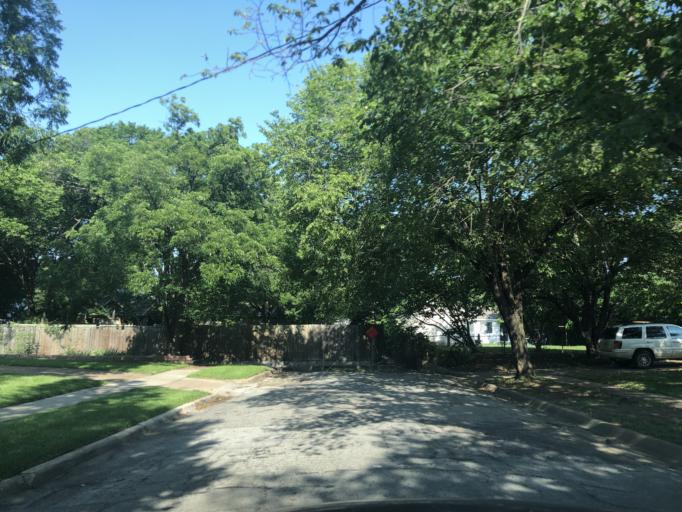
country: US
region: Texas
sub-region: Dallas County
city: Irving
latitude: 32.8108
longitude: -96.9609
